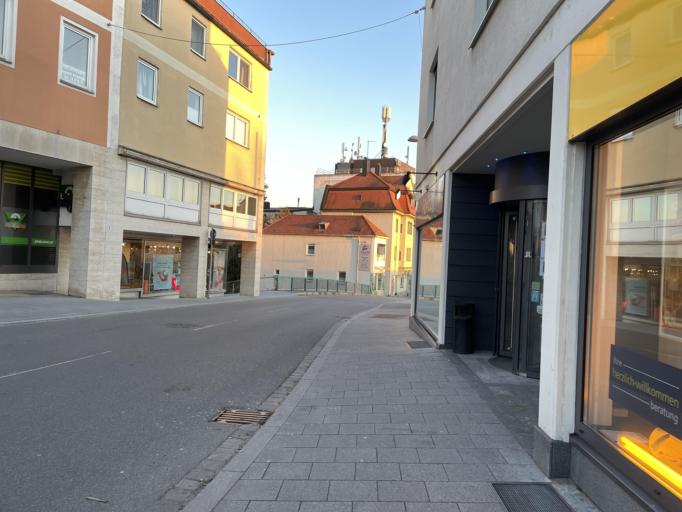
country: DE
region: Bavaria
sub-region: Upper Palatinate
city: Cham
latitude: 49.2202
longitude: 12.6636
